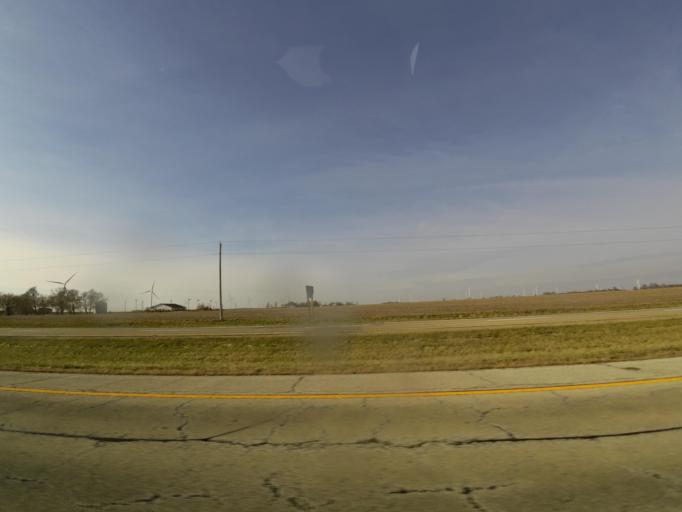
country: US
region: Illinois
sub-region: Macon County
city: Maroa
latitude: 40.0093
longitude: -88.9561
